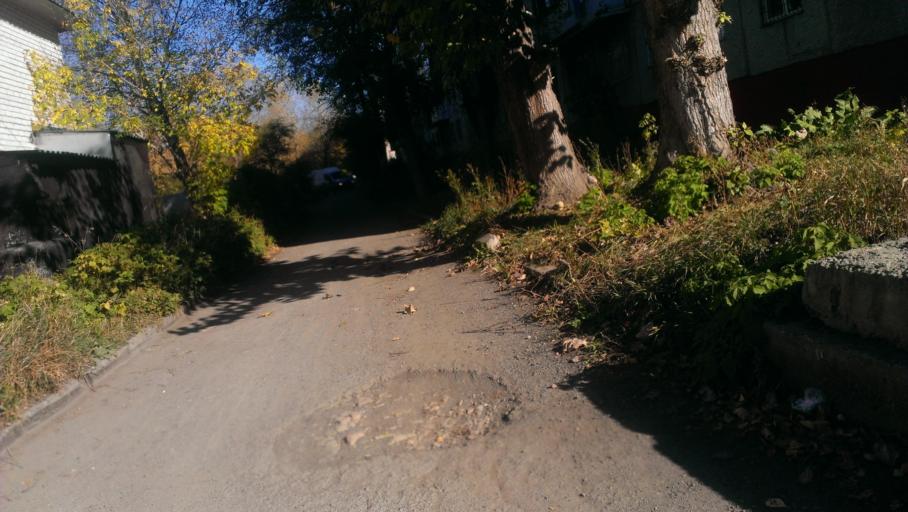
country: RU
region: Altai Krai
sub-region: Gorod Barnaulskiy
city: Barnaul
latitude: 53.3644
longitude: 83.6845
